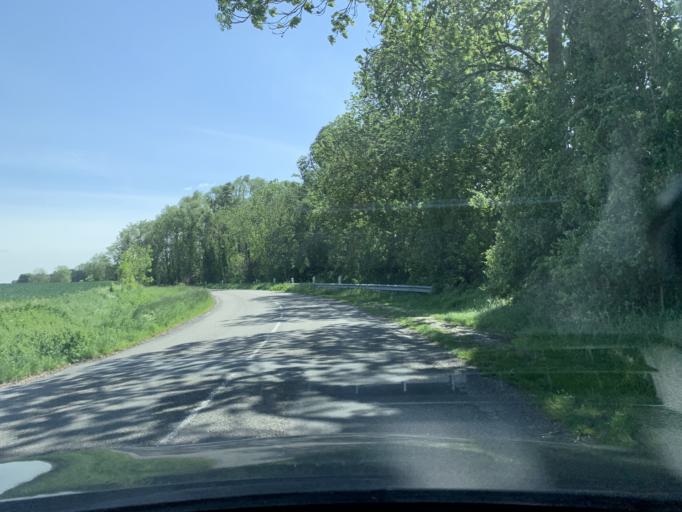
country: FR
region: Nord-Pas-de-Calais
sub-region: Departement du Nord
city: Marcoing
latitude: 50.1383
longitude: 3.1924
